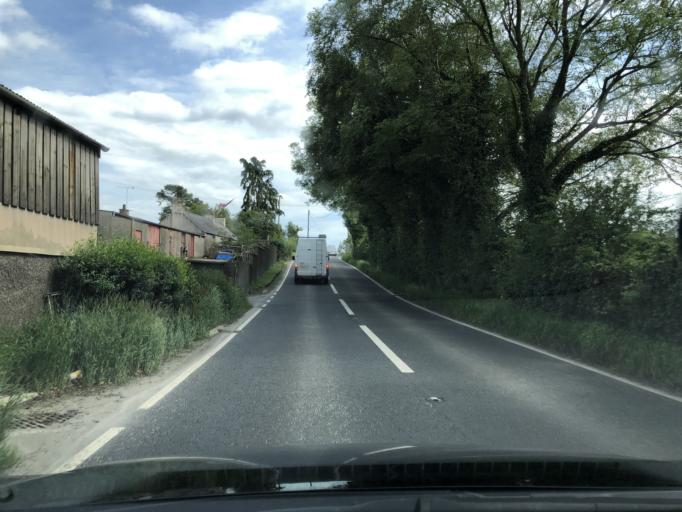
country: GB
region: Northern Ireland
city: Ballynahinch
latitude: 54.4152
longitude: -5.9062
